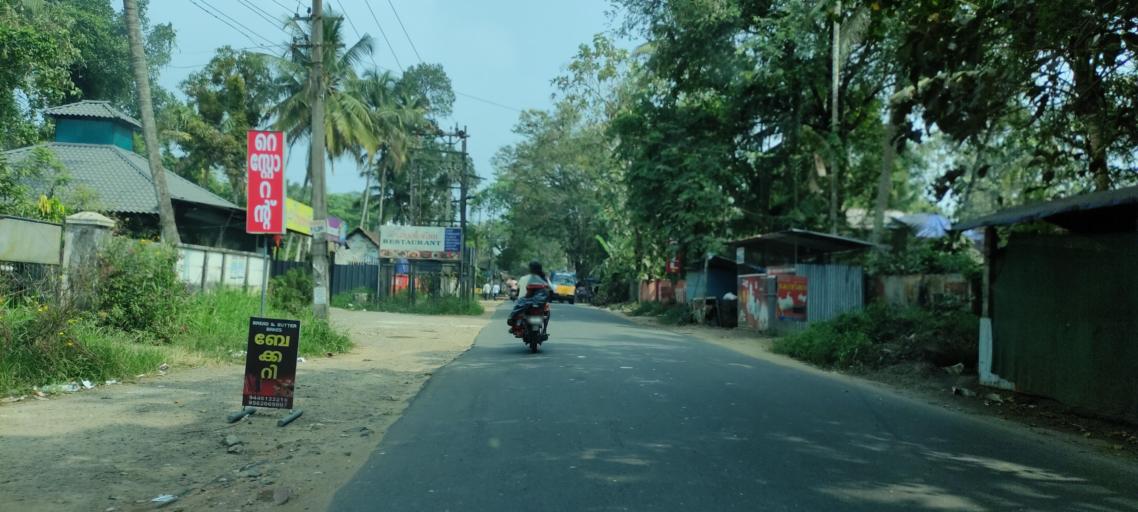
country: IN
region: Kerala
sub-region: Alappuzha
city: Shertallai
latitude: 9.6716
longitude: 76.4075
